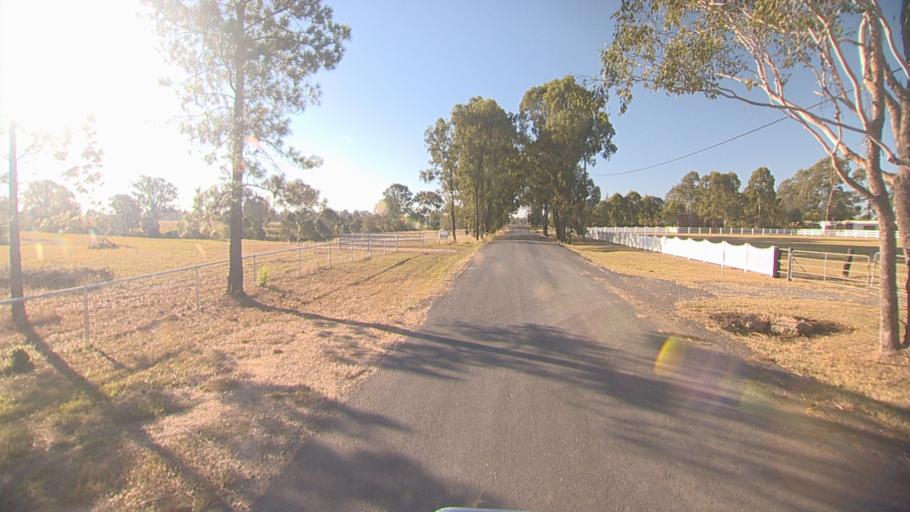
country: AU
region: Queensland
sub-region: Logan
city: North Maclean
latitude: -27.7759
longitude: 153.0474
